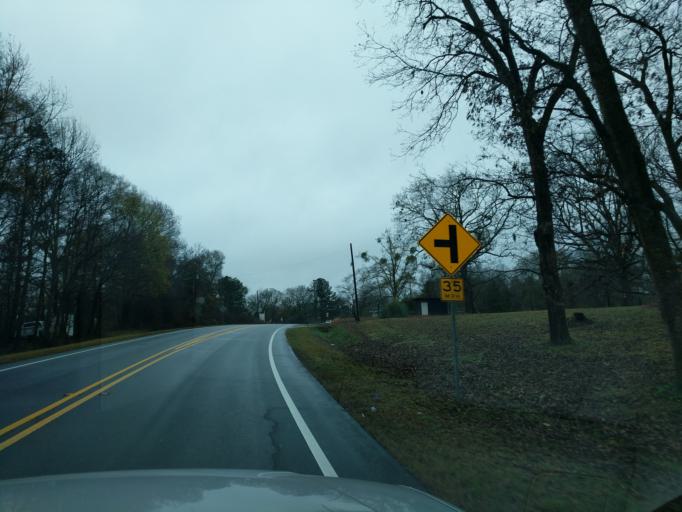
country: US
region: Georgia
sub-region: Franklin County
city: Lavonia
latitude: 34.3760
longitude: -83.0856
